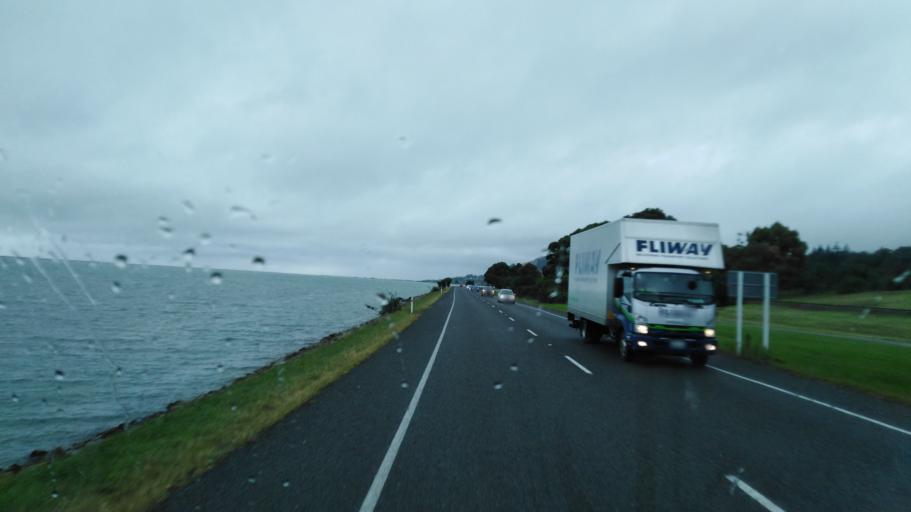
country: NZ
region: Nelson
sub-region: Nelson City
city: Nelson
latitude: -41.2607
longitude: 173.2943
